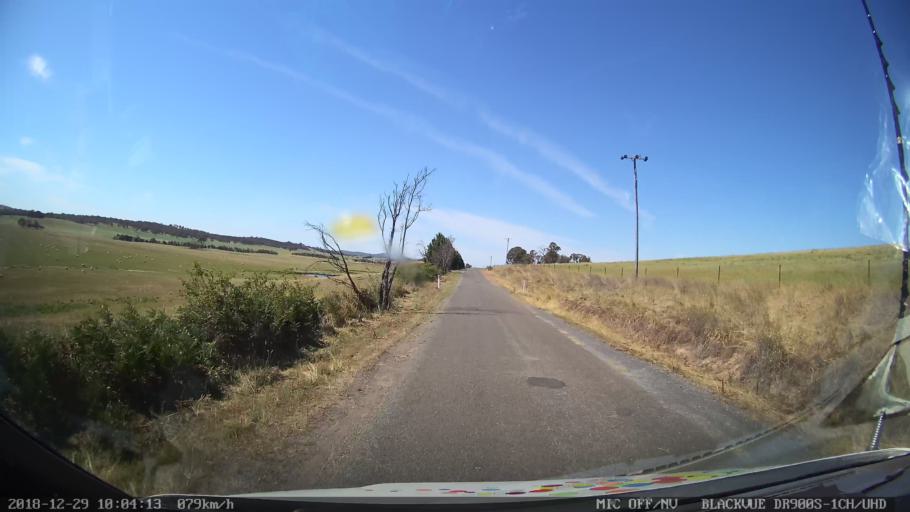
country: AU
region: New South Wales
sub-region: Goulburn Mulwaree
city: Goulburn
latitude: -34.8197
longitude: 149.4558
